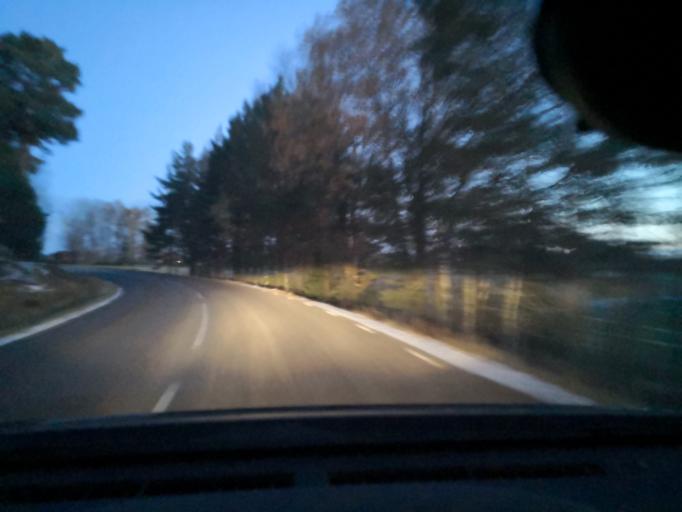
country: SE
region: Vaestmanland
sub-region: Sala Kommun
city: Sala
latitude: 59.8731
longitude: 16.7033
